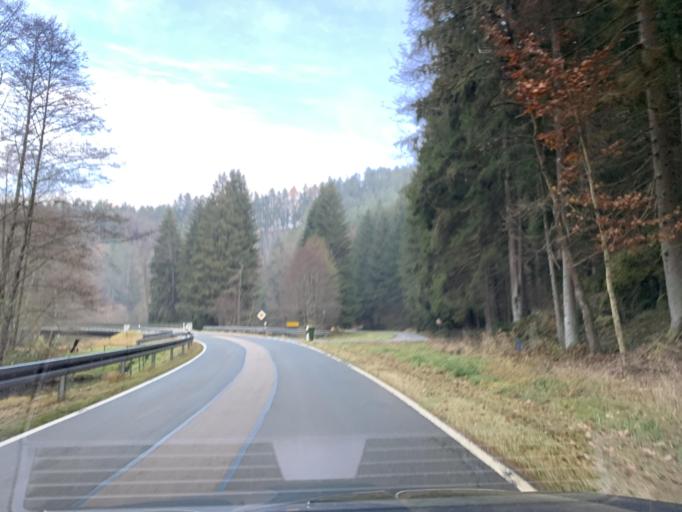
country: DE
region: Bavaria
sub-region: Upper Palatinate
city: Thanstein
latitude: 49.3673
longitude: 12.4318
